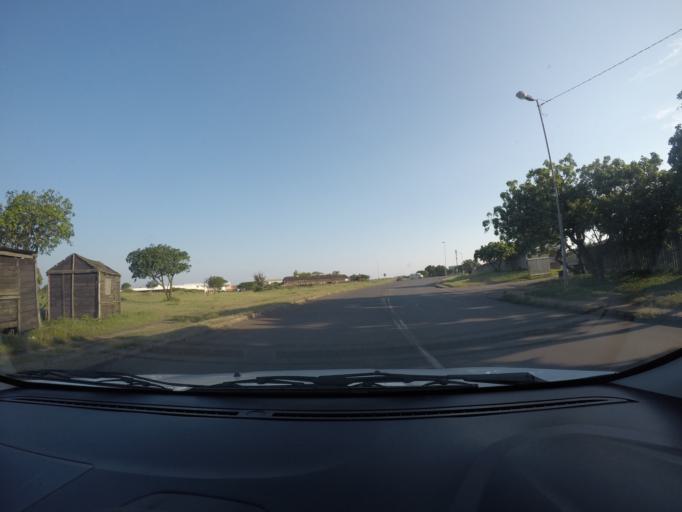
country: ZA
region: KwaZulu-Natal
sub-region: uThungulu District Municipality
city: Richards Bay
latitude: -28.7665
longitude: 32.0094
